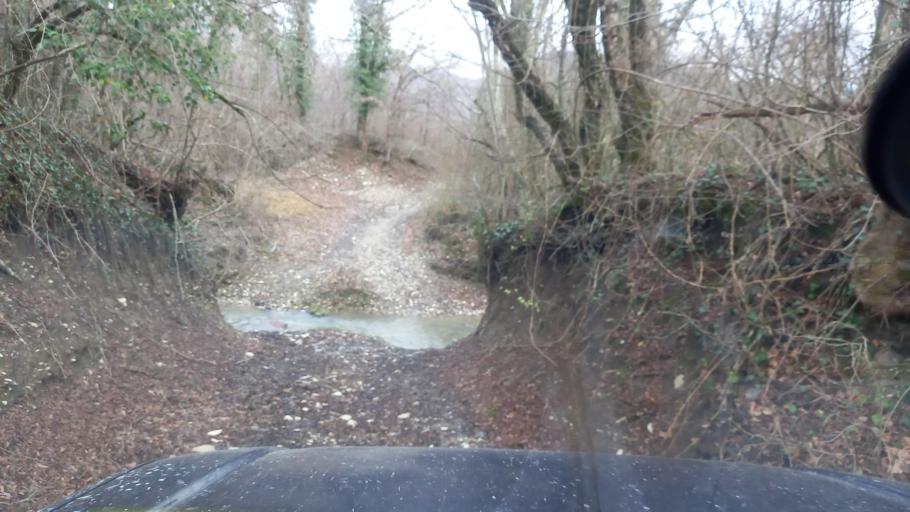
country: RU
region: Krasnodarskiy
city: Pshada
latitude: 44.4929
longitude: 38.4121
